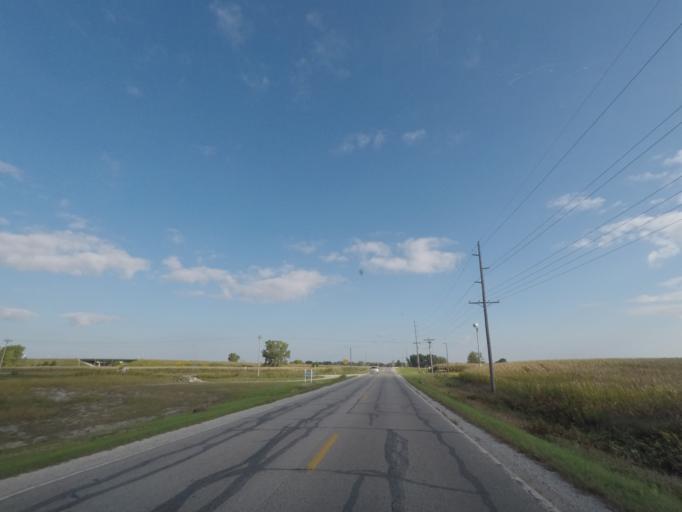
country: US
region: Iowa
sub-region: Story County
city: Nevada
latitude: 42.0038
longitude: -93.4628
